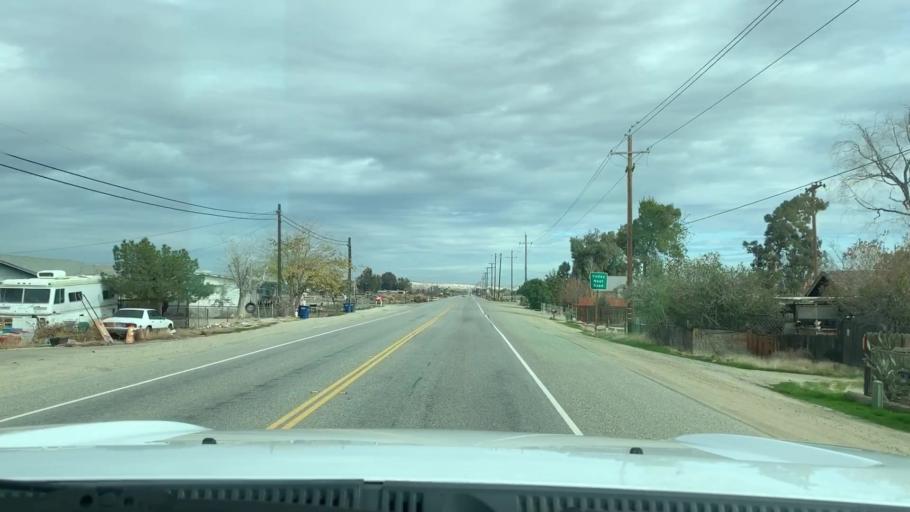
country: US
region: California
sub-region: Kern County
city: Ford City
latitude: 35.2089
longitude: -119.4062
